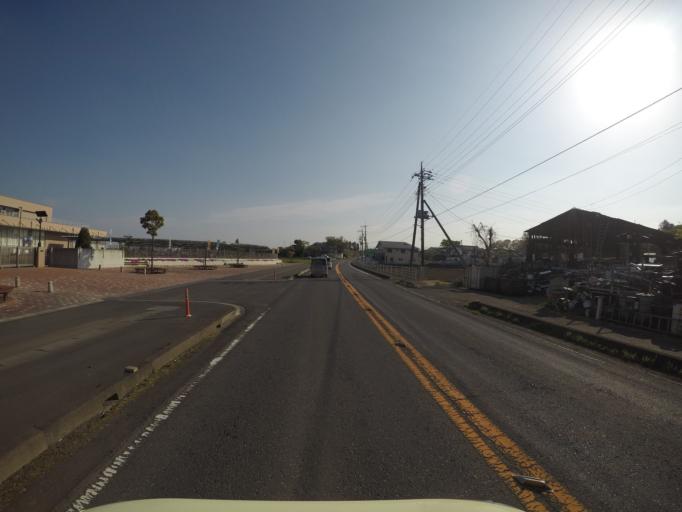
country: JP
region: Ibaraki
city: Ishige
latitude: 36.2012
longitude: 139.9758
